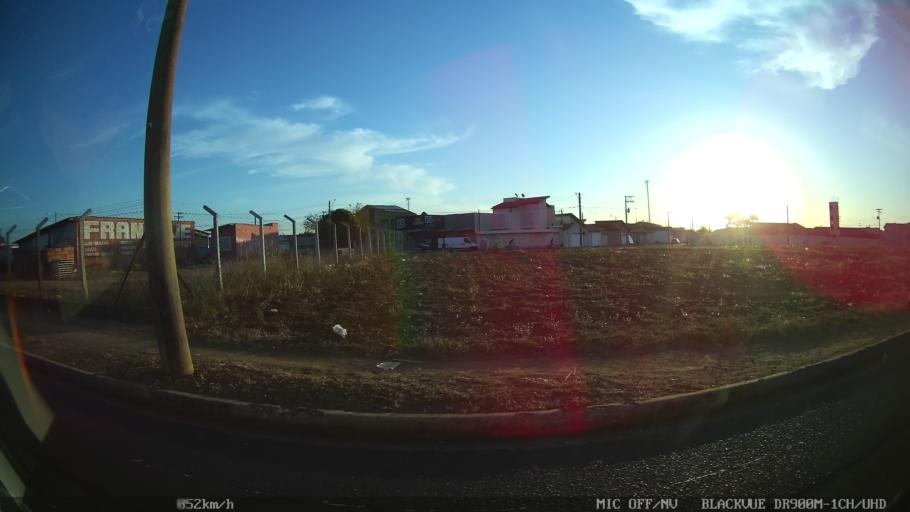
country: BR
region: Sao Paulo
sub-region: Franca
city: Franca
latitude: -20.4938
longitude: -47.4076
